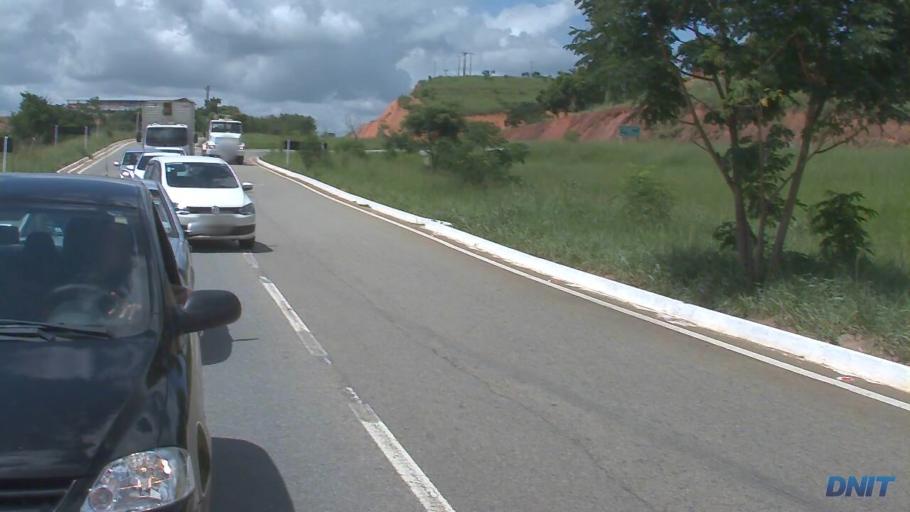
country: BR
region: Minas Gerais
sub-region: Governador Valadares
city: Governador Valadares
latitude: -18.9079
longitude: -42.0050
